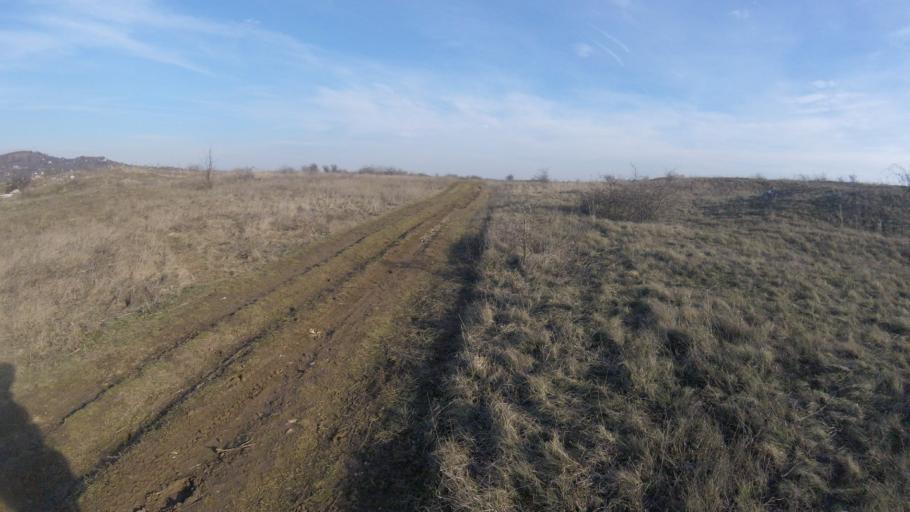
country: HU
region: Pest
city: Nagykovacsi
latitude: 47.6474
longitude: 18.9963
